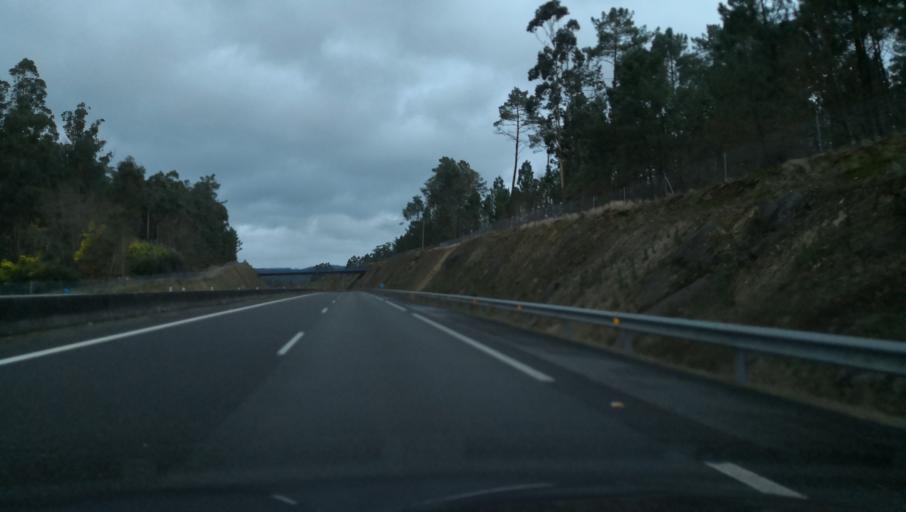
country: ES
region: Galicia
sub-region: Provincia da Coruna
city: Vedra
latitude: 42.8051
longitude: -8.4825
